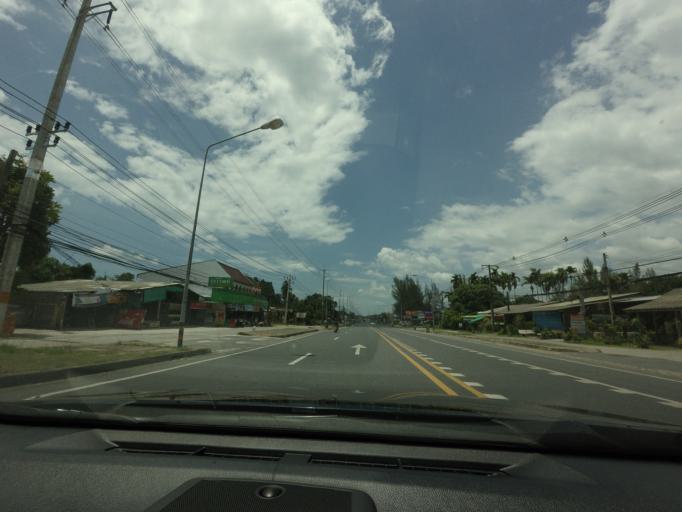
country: TH
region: Phangnga
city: Ban Khao Lak
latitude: 8.6597
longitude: 98.2533
